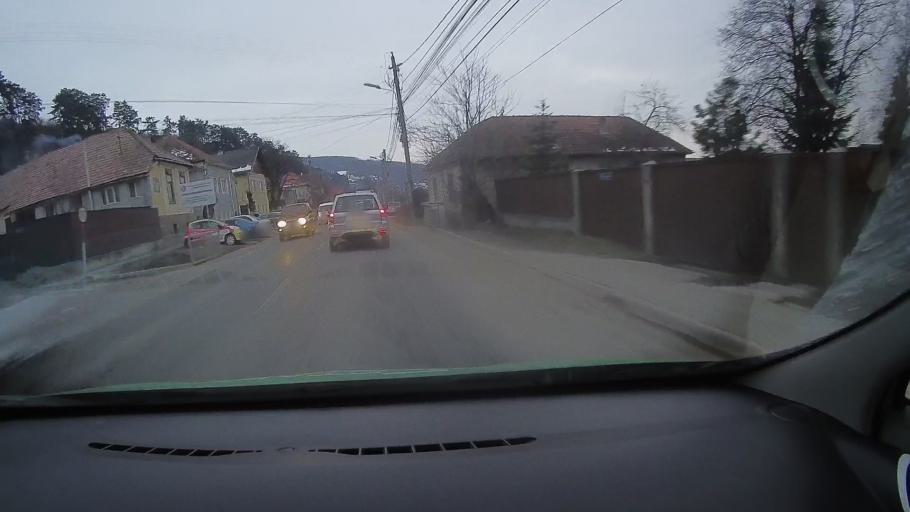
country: RO
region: Harghita
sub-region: Municipiul Odorheiu Secuiesc
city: Odorheiu Secuiesc
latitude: 46.2946
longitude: 25.2894
